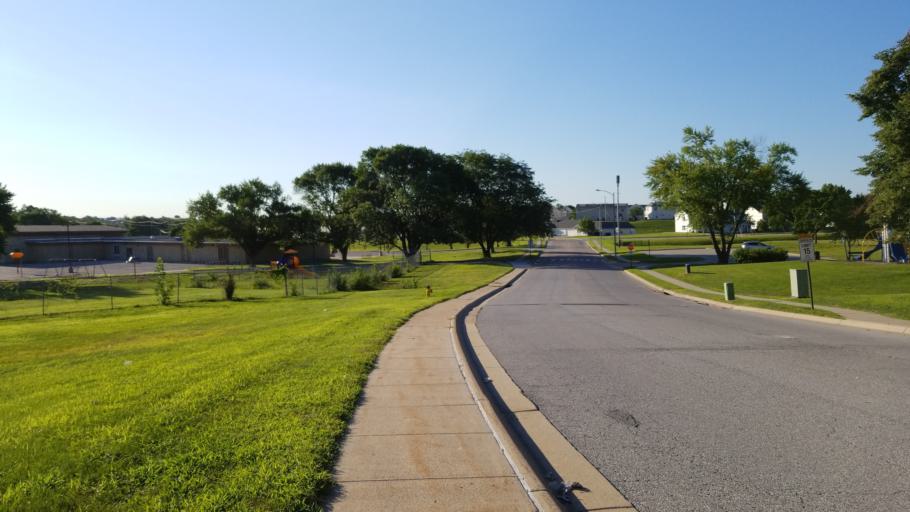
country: US
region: Nebraska
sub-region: Sarpy County
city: Offutt Air Force Base
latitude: 41.1304
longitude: -95.9536
